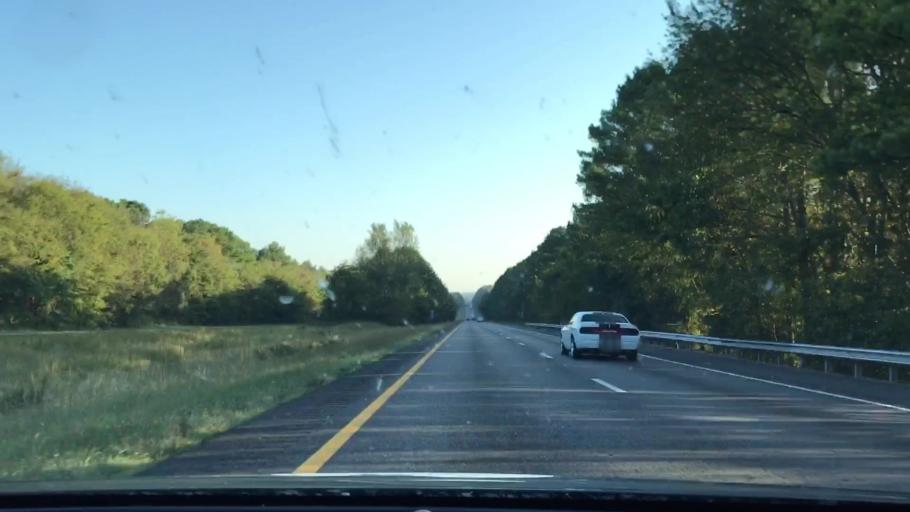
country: US
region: Tennessee
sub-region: Robertson County
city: Cross Plains
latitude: 36.5581
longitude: -86.6267
